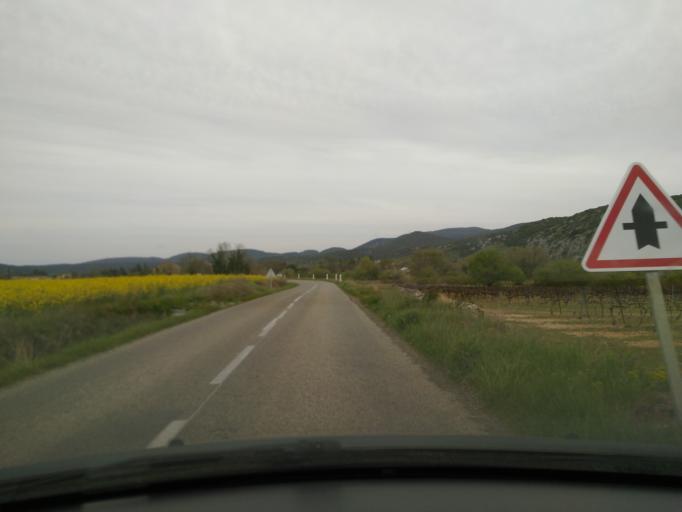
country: FR
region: Rhone-Alpes
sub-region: Departement de l'Ardeche
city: Ruoms
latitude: 44.4116
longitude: 4.4070
